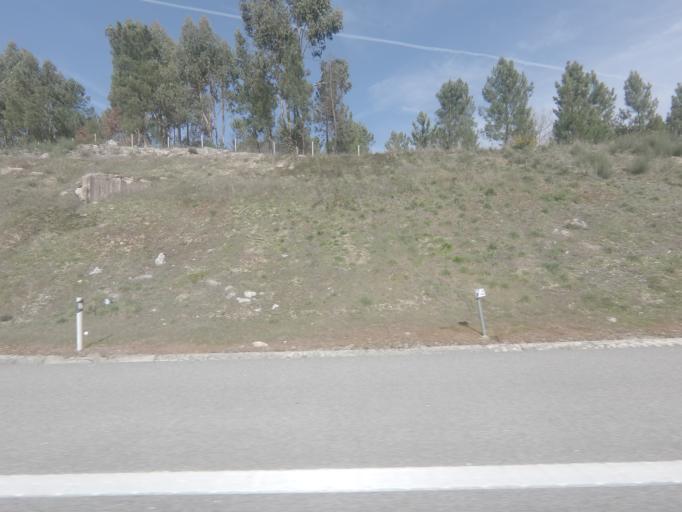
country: PT
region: Viseu
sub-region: Viseu
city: Abraveses
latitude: 40.6302
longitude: -7.9982
